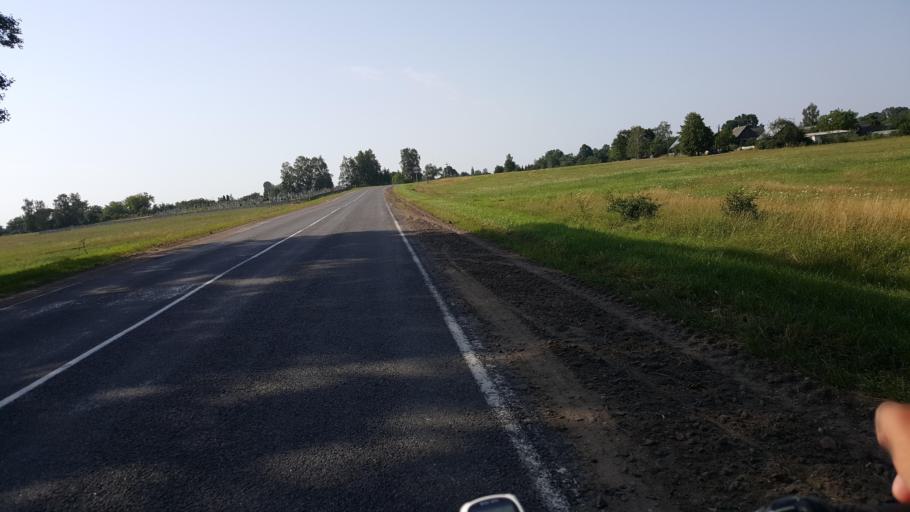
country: BY
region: Brest
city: Zhabinka
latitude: 52.3082
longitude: 23.9244
